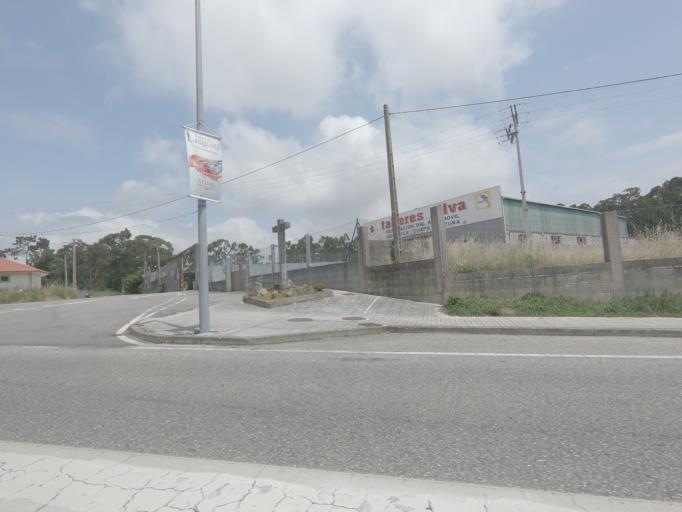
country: ES
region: Galicia
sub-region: Provincia de Pontevedra
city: A Guarda
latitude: 41.8970
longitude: -8.8595
